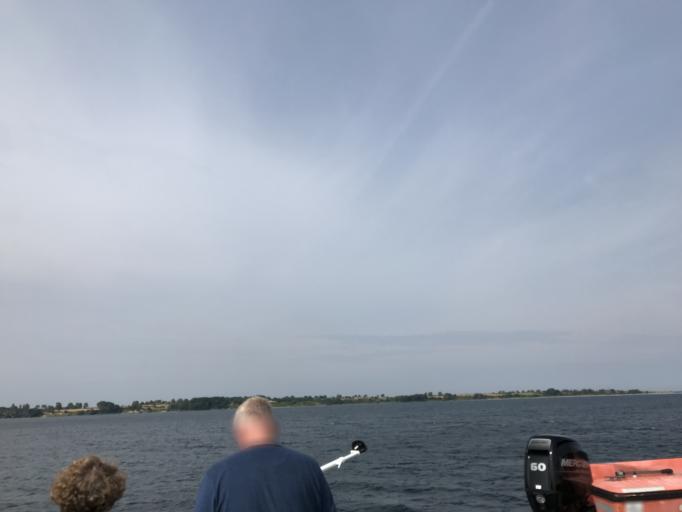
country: DK
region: South Denmark
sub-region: Faaborg-Midtfyn Kommune
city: Faaborg
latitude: 54.9624
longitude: 10.2530
